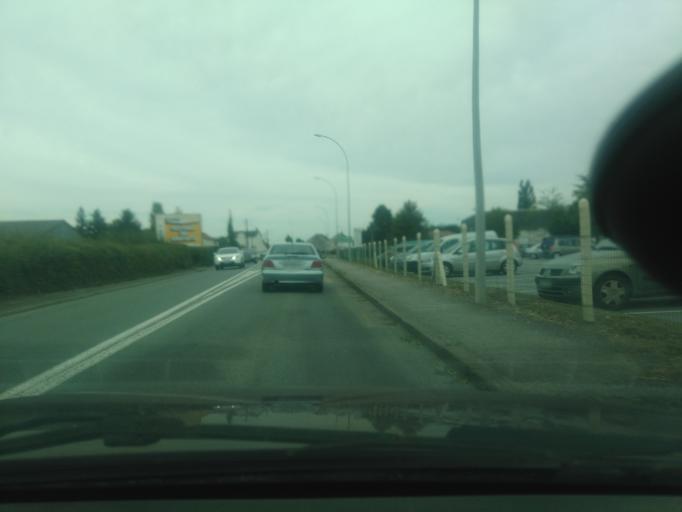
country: FR
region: Poitou-Charentes
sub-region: Departement des Deux-Sevres
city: Parthenay
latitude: 46.6375
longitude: -0.2432
